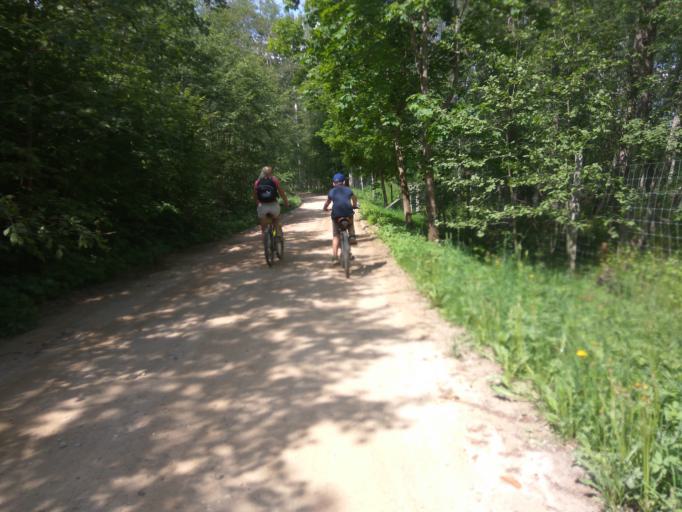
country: LV
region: Kuldigas Rajons
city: Kuldiga
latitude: 56.8838
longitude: 21.9304
